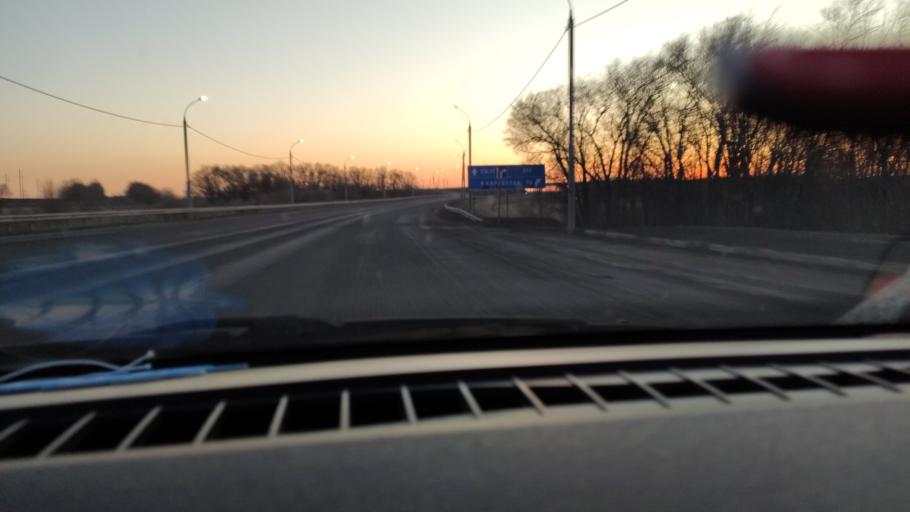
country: RU
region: Saratov
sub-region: Saratovskiy Rayon
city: Saratov
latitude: 51.7723
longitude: 46.0860
